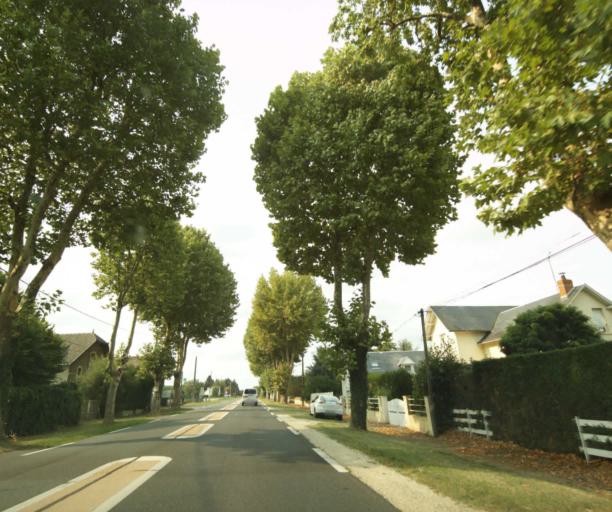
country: FR
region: Centre
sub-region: Departement de l'Indre
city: Chatillon-sur-Indre
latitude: 47.0223
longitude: 1.1056
